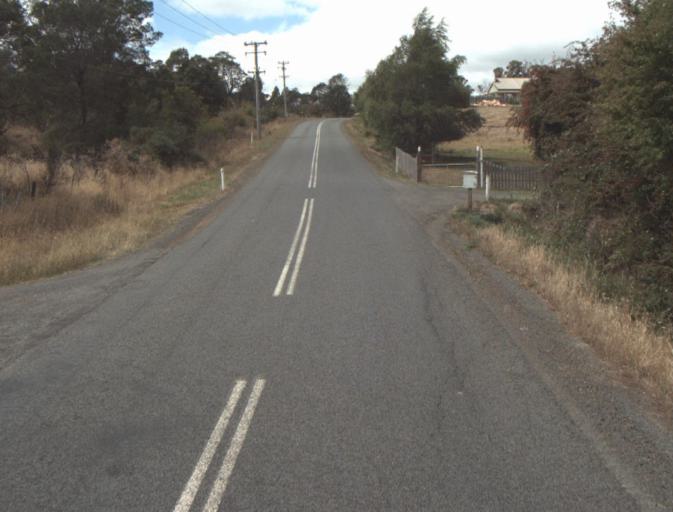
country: AU
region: Tasmania
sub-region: Northern Midlands
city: Evandale
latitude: -41.5079
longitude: 147.2752
